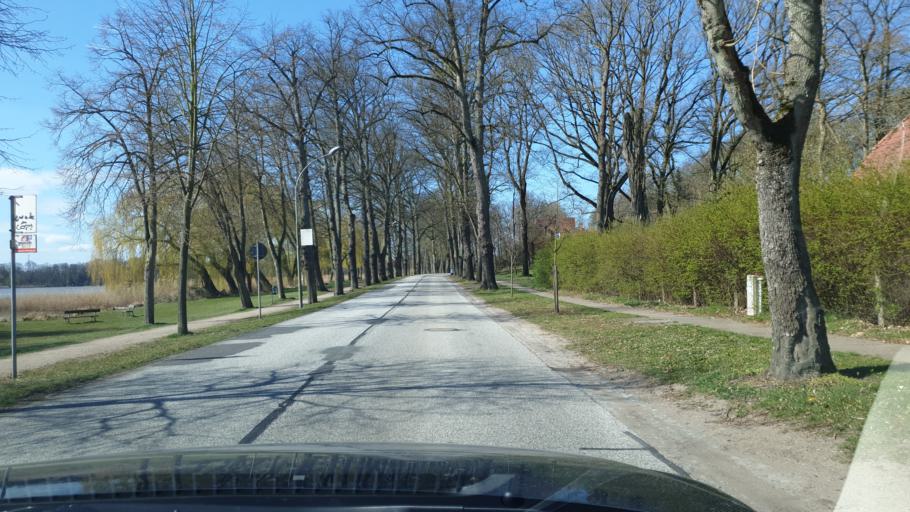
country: DE
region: Mecklenburg-Vorpommern
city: Crivitz
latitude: 53.5809
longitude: 11.6449
